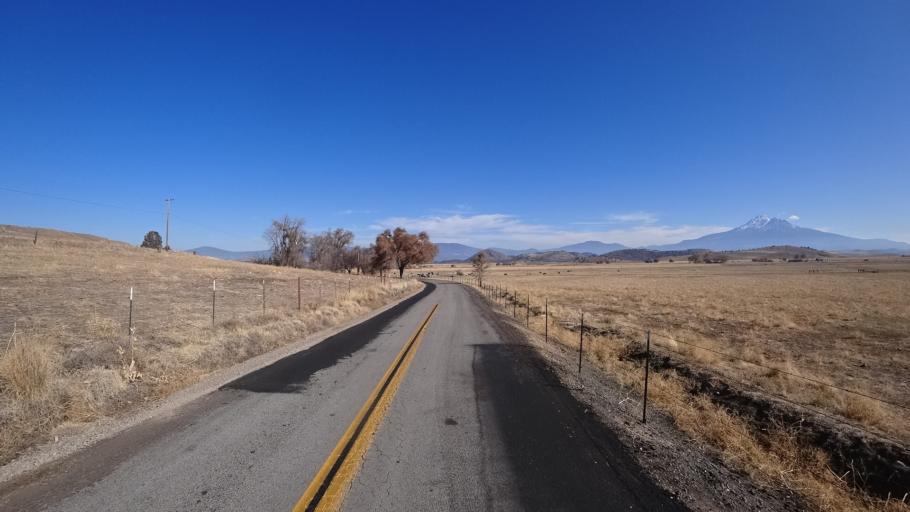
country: US
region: California
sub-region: Siskiyou County
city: Montague
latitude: 41.5995
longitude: -122.5332
